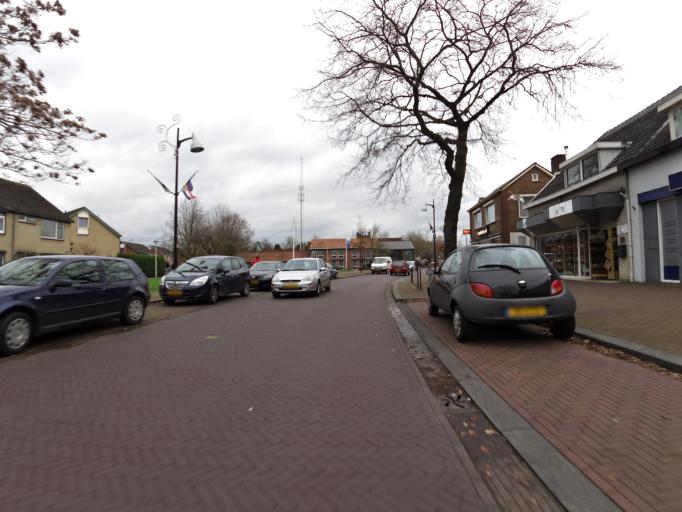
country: NL
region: Gelderland
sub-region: Gemeente Zevenaar
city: Zevenaar
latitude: 51.9431
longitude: 6.1289
